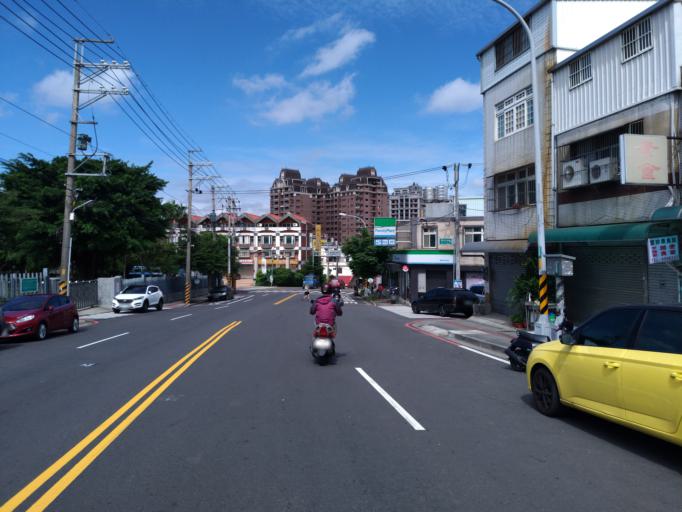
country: TW
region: Taiwan
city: Taoyuan City
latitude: 24.9563
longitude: 121.1674
